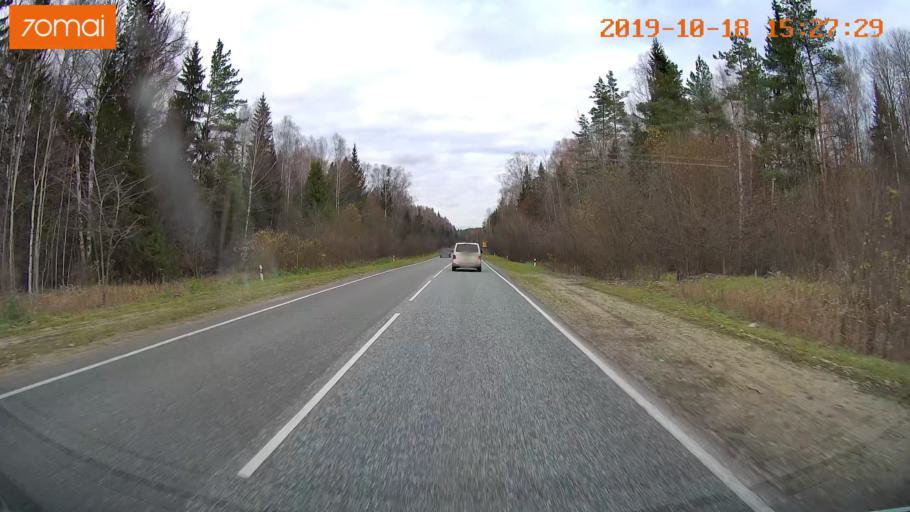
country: RU
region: Vladimir
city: Anopino
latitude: 55.7539
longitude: 40.6712
